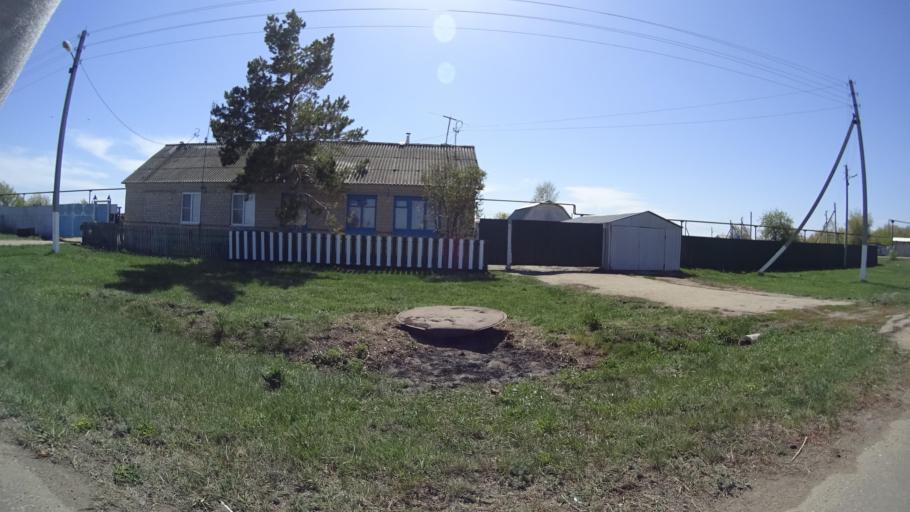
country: RU
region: Chelyabinsk
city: Chesma
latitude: 53.7922
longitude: 61.0382
